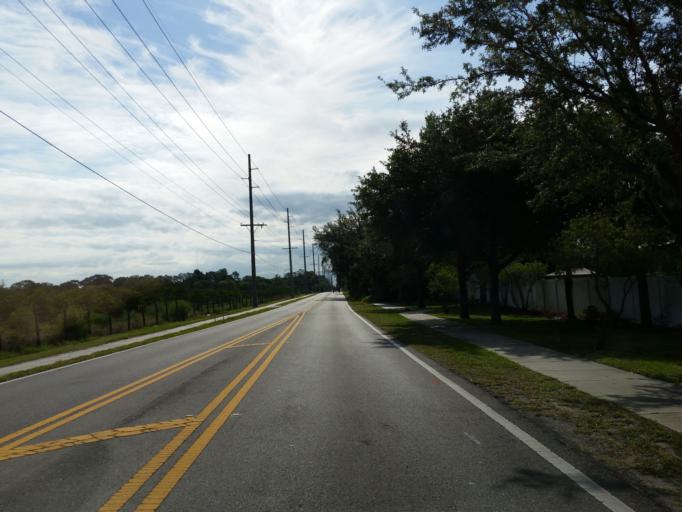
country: US
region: Florida
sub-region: Hillsborough County
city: Riverview
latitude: 27.8352
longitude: -82.3401
